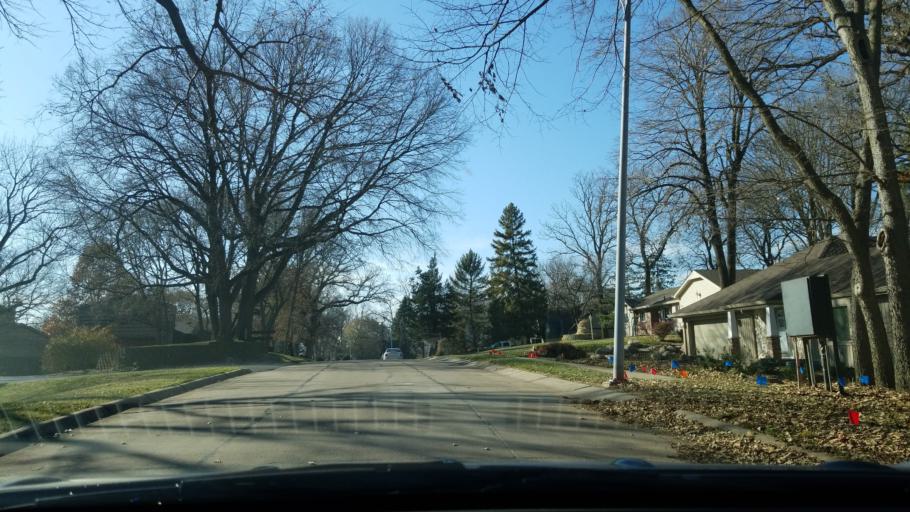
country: US
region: Nebraska
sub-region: Sarpy County
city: Bellevue
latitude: 41.1639
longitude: -95.8983
